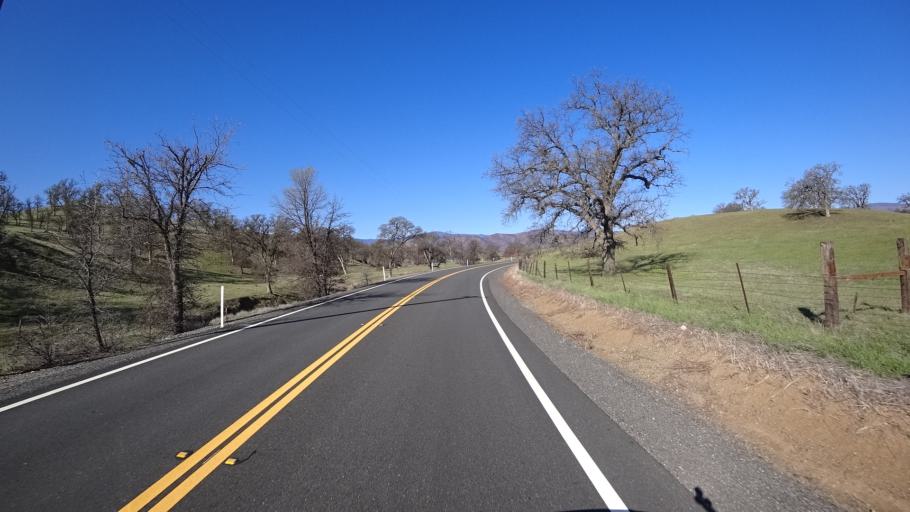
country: US
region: California
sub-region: Glenn County
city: Orland
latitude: 39.6598
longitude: -122.5363
